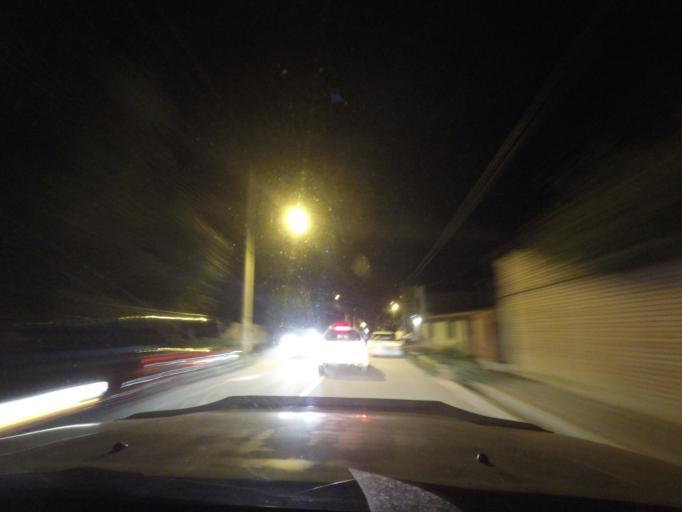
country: BO
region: Cochabamba
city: Cochabamba
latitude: -17.3772
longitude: -66.2030
